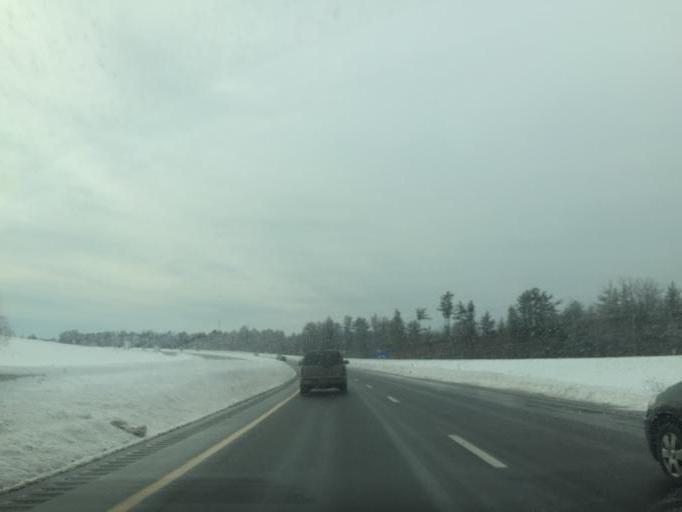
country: US
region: New Hampshire
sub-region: Strafford County
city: Rochester
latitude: 43.3188
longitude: -70.9955
